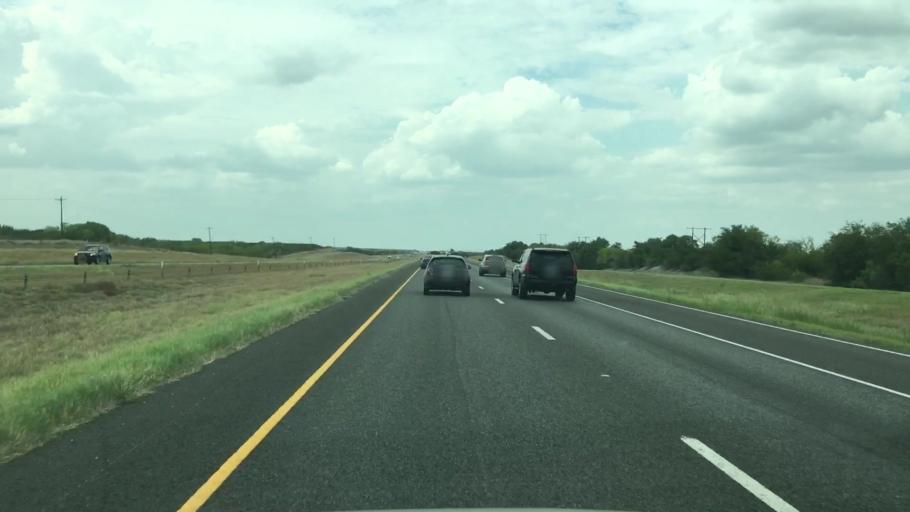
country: US
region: Texas
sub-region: Atascosa County
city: Pleasanton
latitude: 28.8330
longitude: -98.3704
